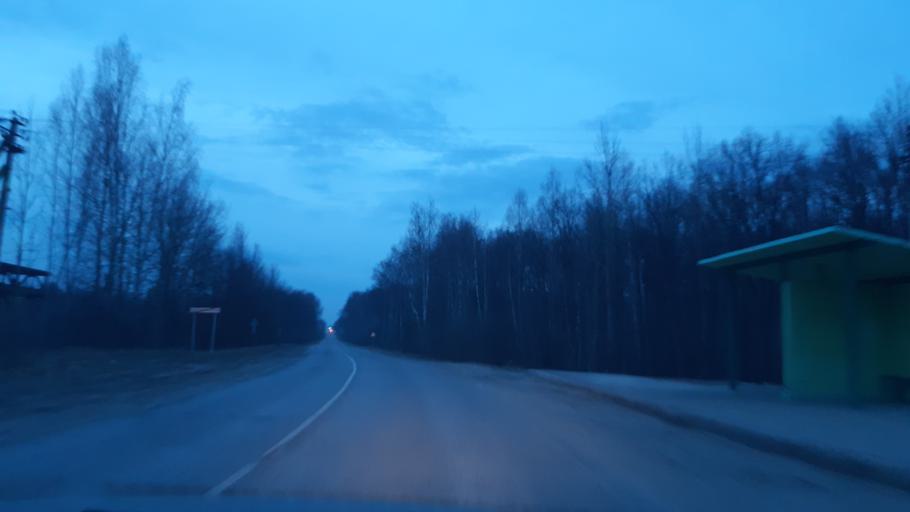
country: RU
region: Vladimir
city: Luknovo
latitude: 56.2238
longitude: 42.0349
